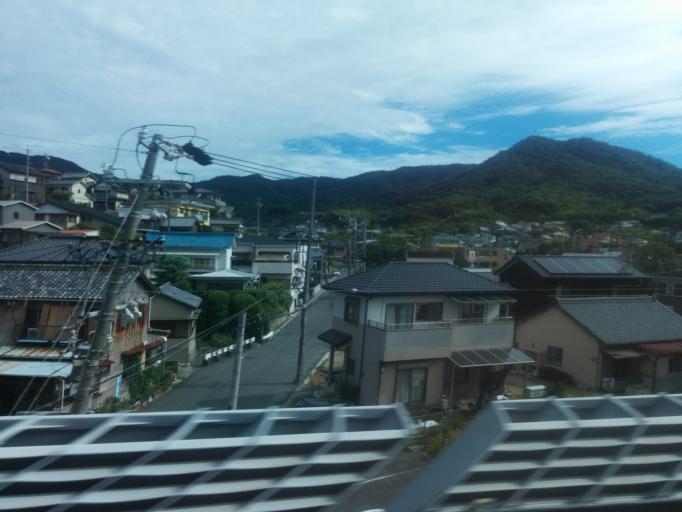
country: JP
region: Aichi
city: Gamagori
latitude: 34.8183
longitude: 137.2554
